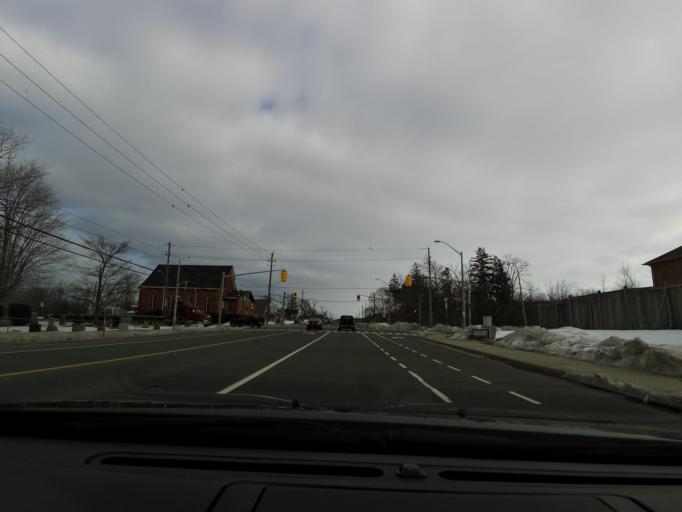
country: CA
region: Ontario
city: Hamilton
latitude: 43.2135
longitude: -79.7044
